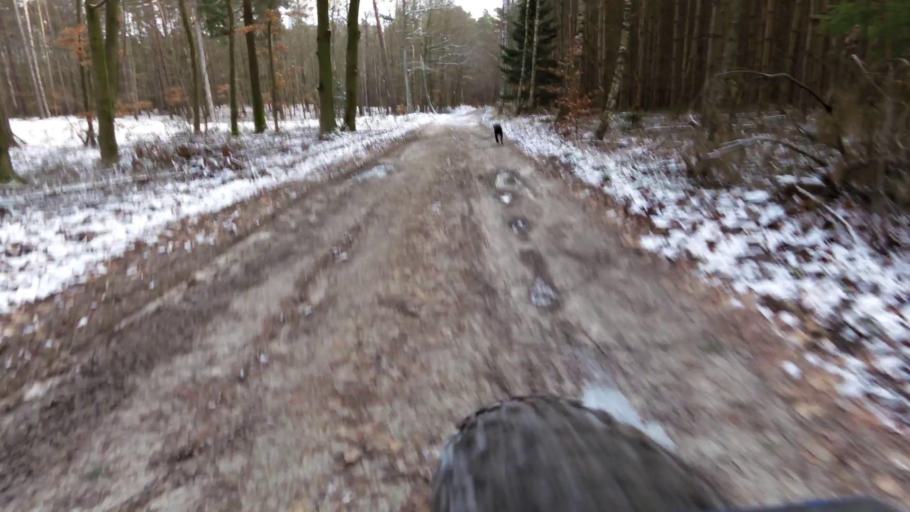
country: PL
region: West Pomeranian Voivodeship
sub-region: Powiat walecki
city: Walcz
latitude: 53.2782
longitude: 16.3070
